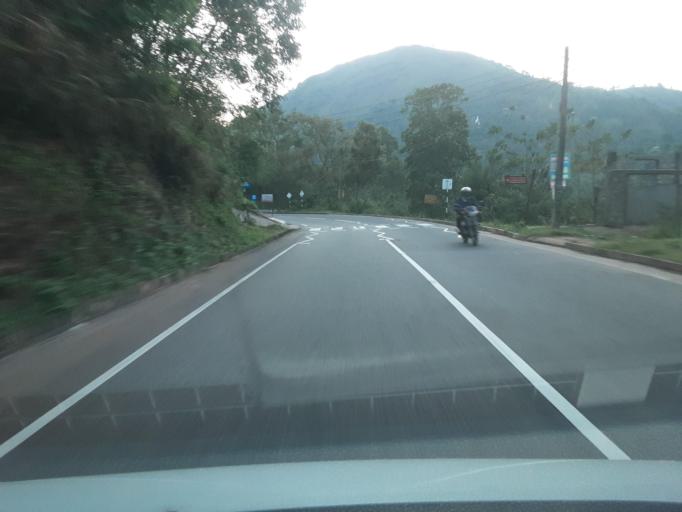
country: LK
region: Uva
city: Badulla
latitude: 6.9204
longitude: 80.9599
